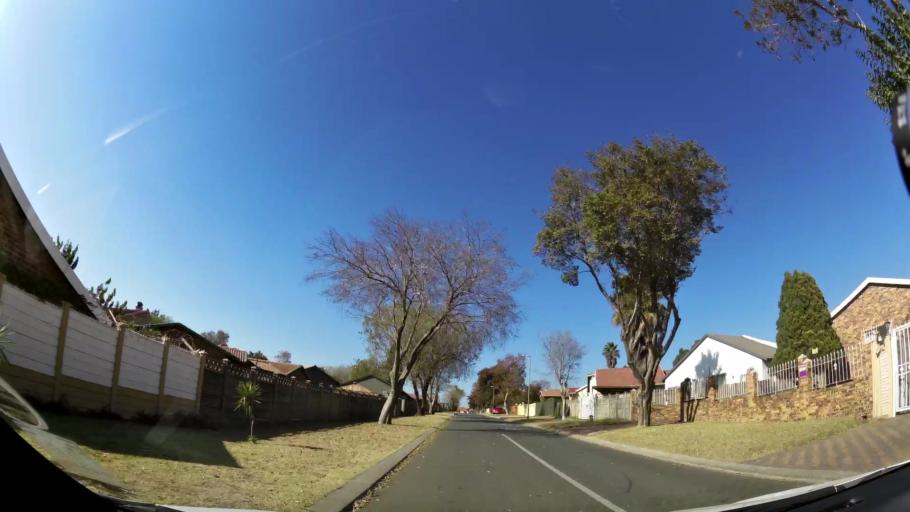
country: ZA
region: Gauteng
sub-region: City of Johannesburg Metropolitan Municipality
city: Johannesburg
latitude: -26.2394
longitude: 28.1007
